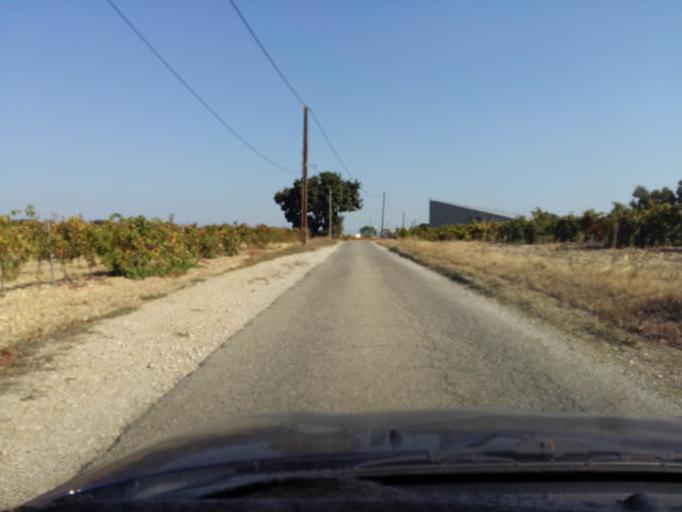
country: FR
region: Provence-Alpes-Cote d'Azur
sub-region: Departement du Vaucluse
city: Sainte-Cecile-les-Vignes
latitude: 44.2289
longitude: 4.8771
